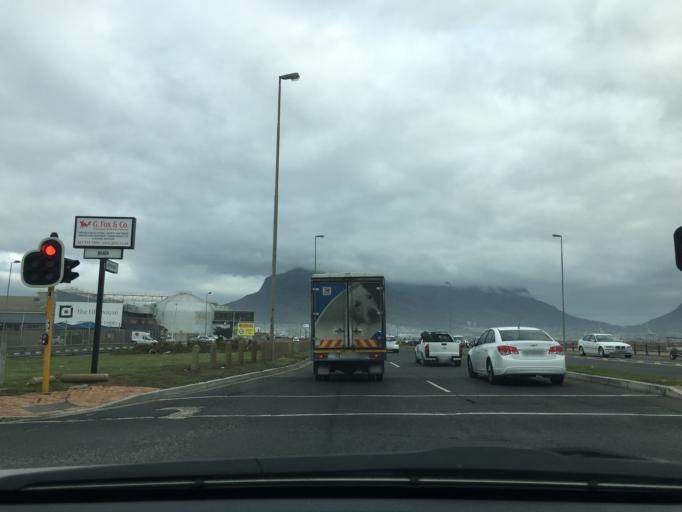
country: ZA
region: Western Cape
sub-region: City of Cape Town
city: Sunset Beach
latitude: -33.9000
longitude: 18.4787
